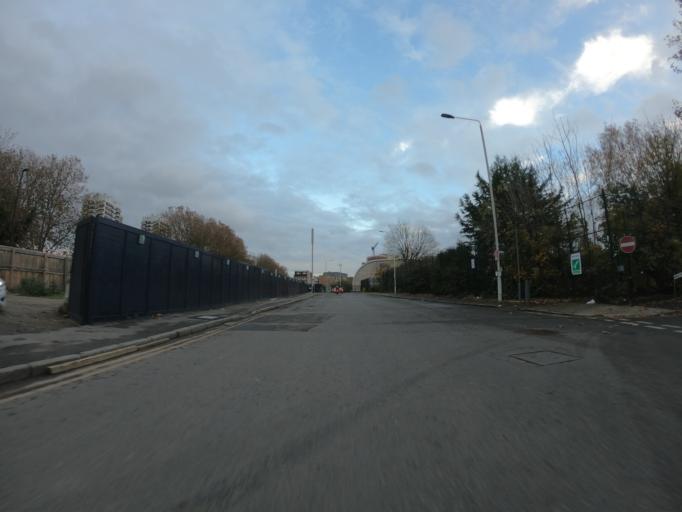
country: GB
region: England
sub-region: Greater London
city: Woolwich
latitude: 51.5003
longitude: 0.0584
